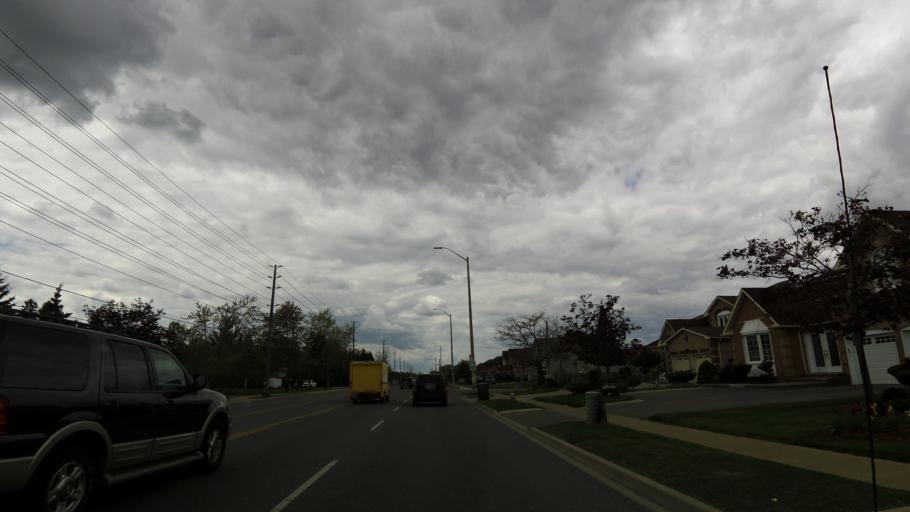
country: CA
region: Ontario
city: Mississauga
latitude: 43.5826
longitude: -79.6915
